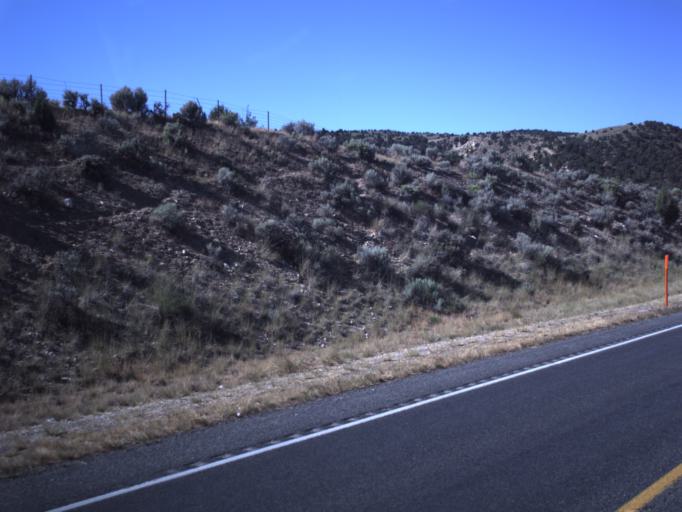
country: US
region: Utah
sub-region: Sanpete County
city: Manti
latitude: 39.2469
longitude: -111.6478
